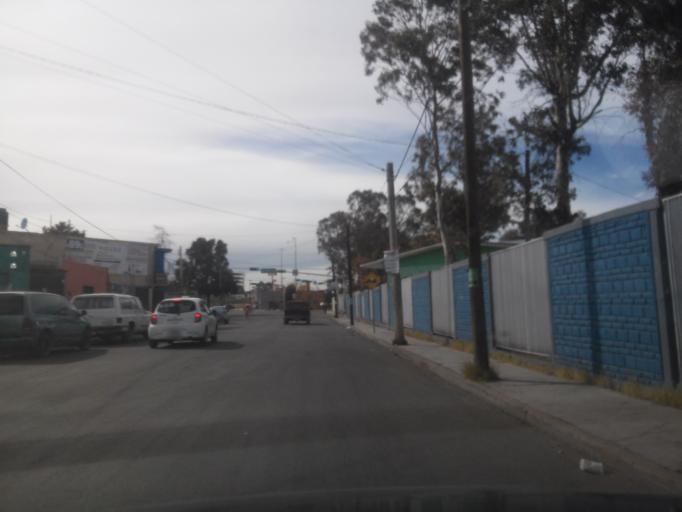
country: MX
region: Durango
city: Victoria de Durango
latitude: 24.0075
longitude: -104.6575
